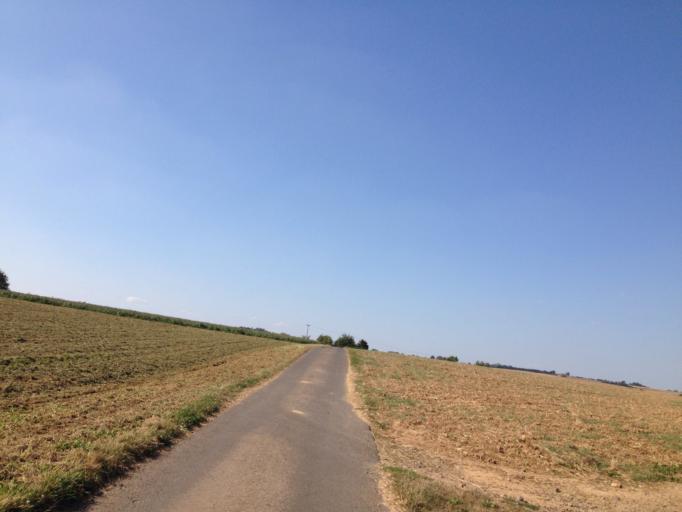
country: DE
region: Hesse
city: Staufenberg
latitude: 50.6542
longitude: 8.7516
